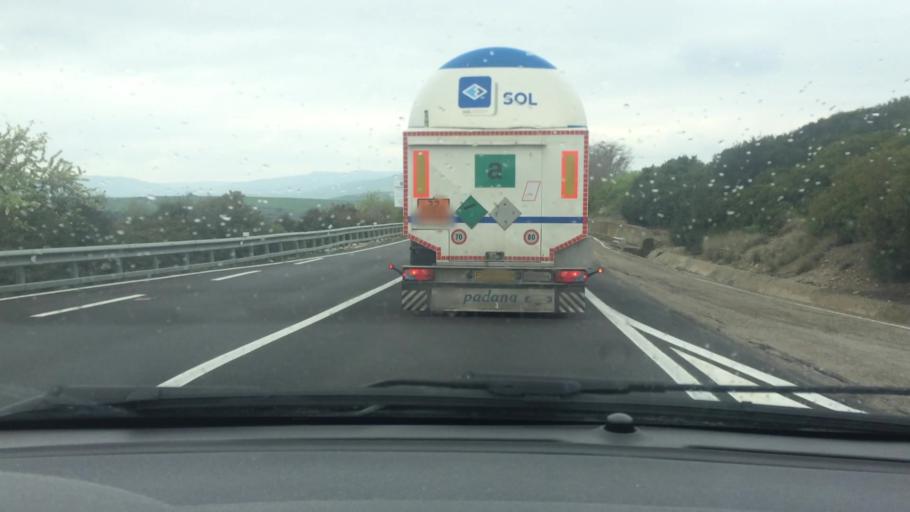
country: IT
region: Basilicate
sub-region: Provincia di Matera
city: Matera
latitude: 40.6206
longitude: 16.5838
